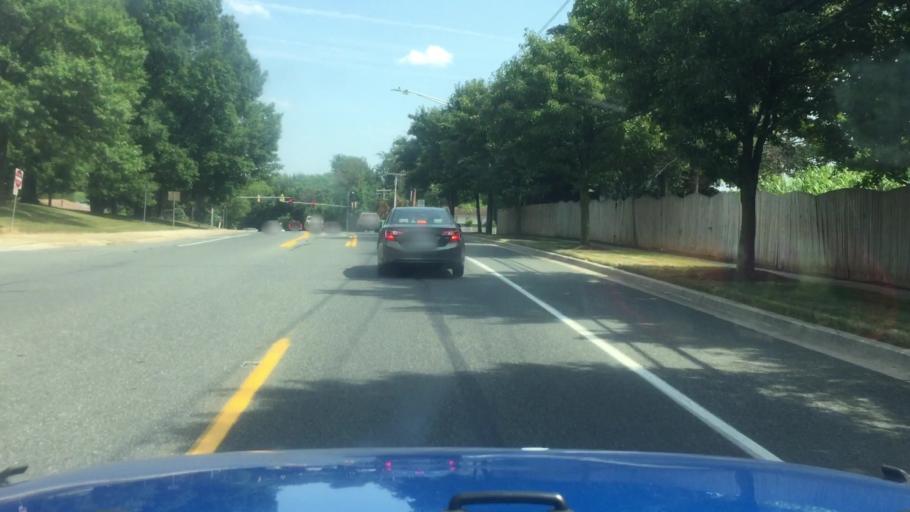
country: US
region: Maryland
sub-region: Anne Arundel County
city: Odenton
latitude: 39.0529
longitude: -76.6958
